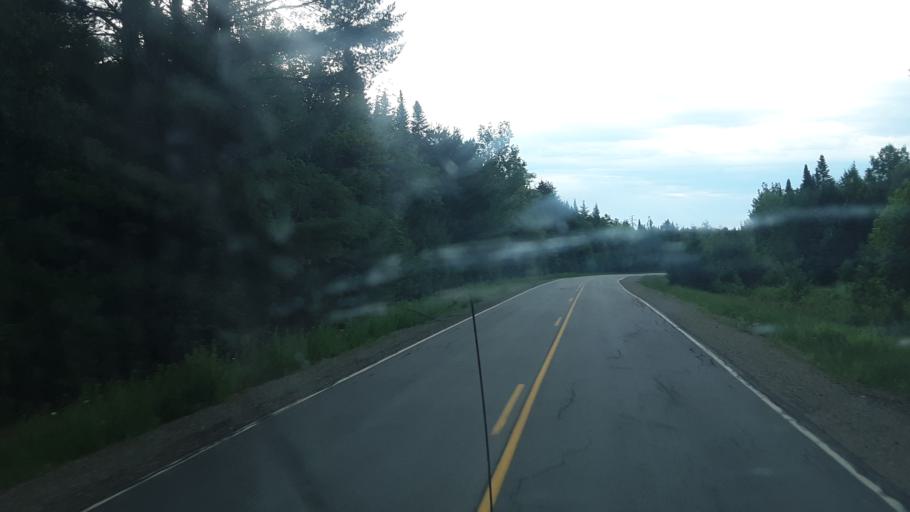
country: US
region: Maine
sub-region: Penobscot County
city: Medway
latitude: 45.6825
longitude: -68.2807
